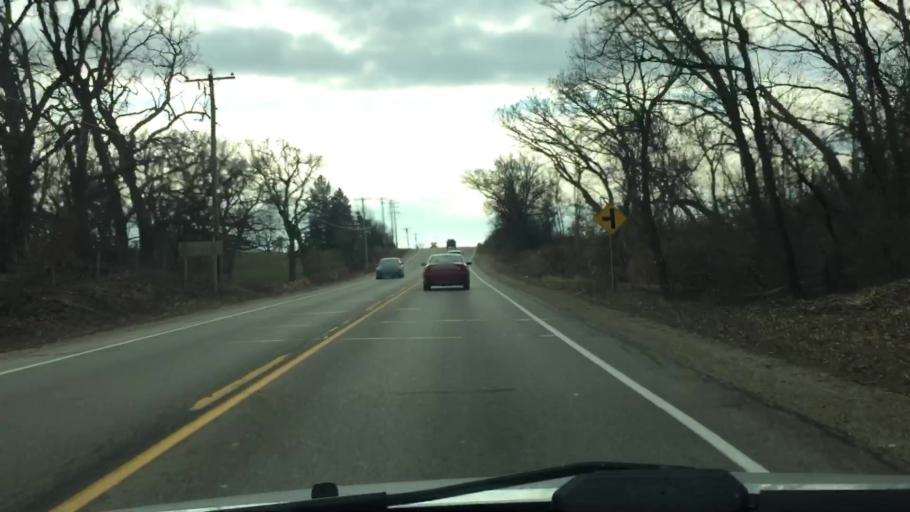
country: US
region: Wisconsin
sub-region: Walworth County
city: Elkhorn
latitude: 42.7221
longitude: -88.5426
